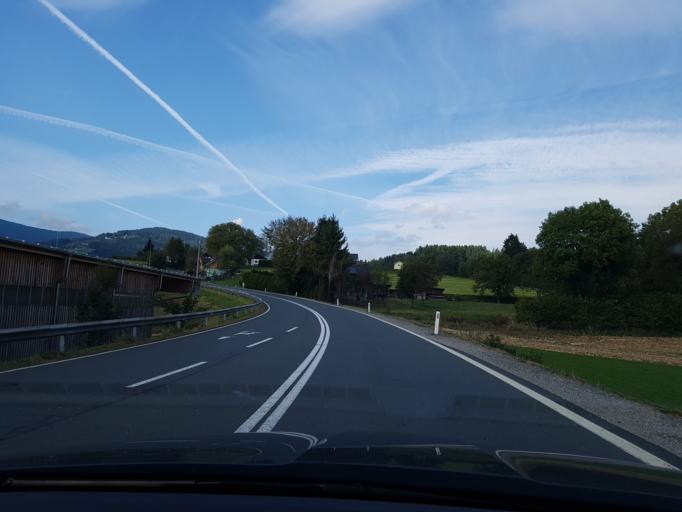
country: AT
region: Carinthia
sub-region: Politischer Bezirk Feldkirchen
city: Feldkirchen in Karnten
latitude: 46.7358
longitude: 14.0703
